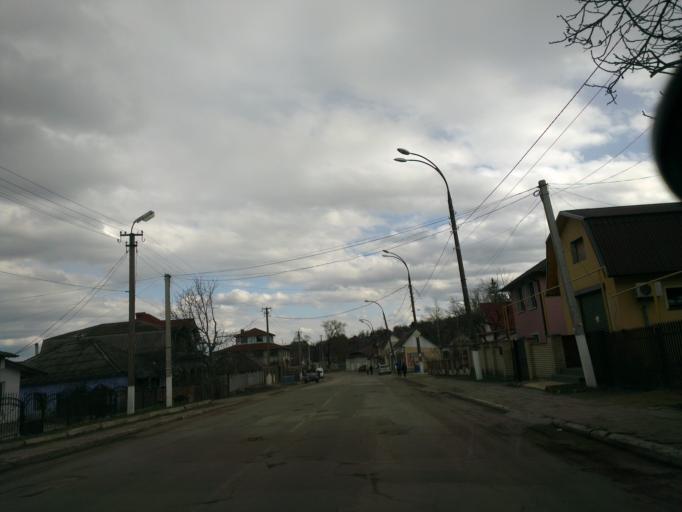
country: MD
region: Hincesti
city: Hincesti
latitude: 46.8209
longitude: 28.5987
